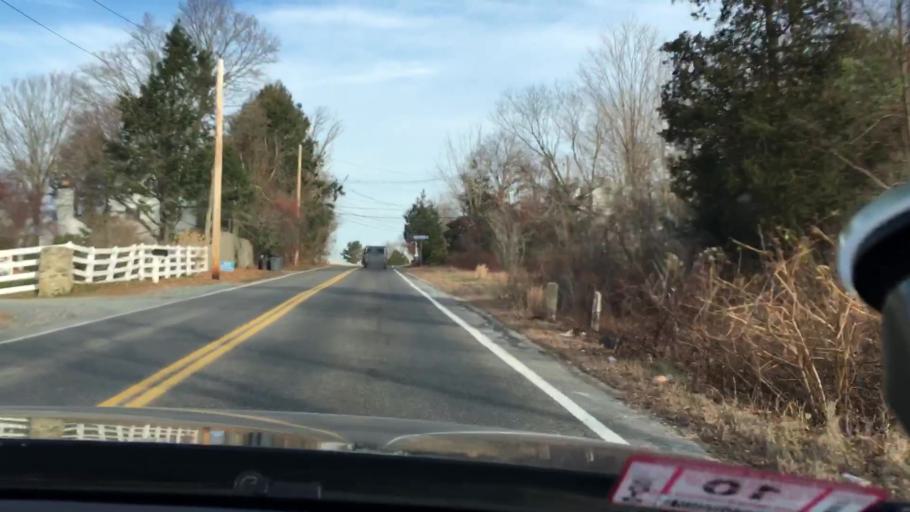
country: US
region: Massachusetts
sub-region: Norfolk County
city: Westwood
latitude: 42.1939
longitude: -71.2494
